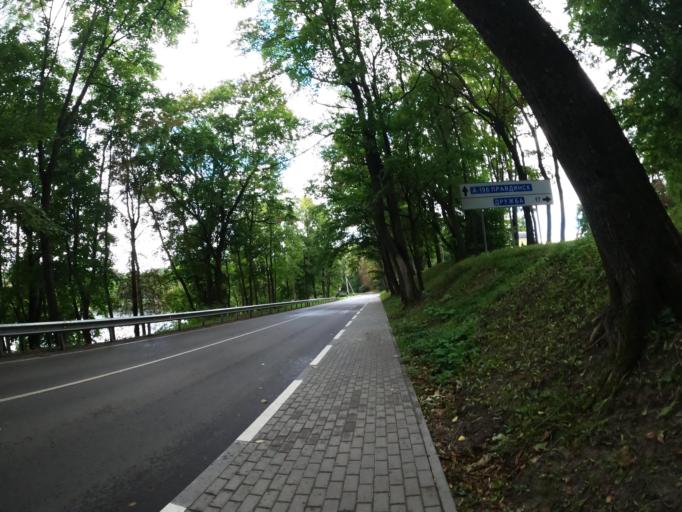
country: RU
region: Kaliningrad
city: Zheleznodorozhnyy
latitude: 54.3622
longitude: 21.3110
